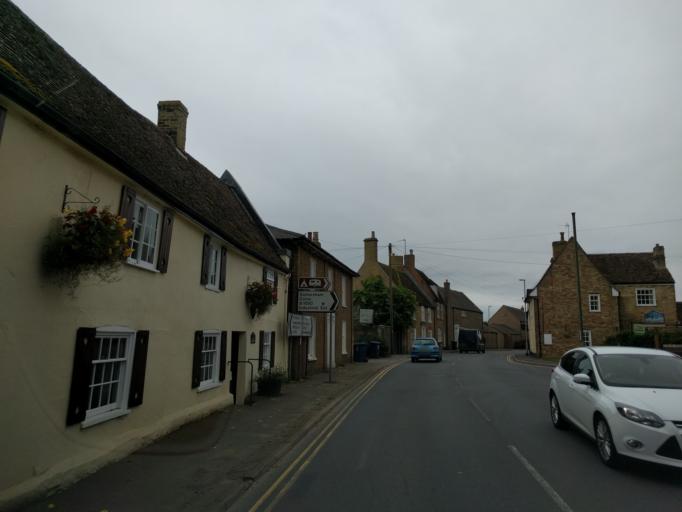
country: GB
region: England
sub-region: Cambridgeshire
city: Earith
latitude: 52.3538
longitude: 0.0315
